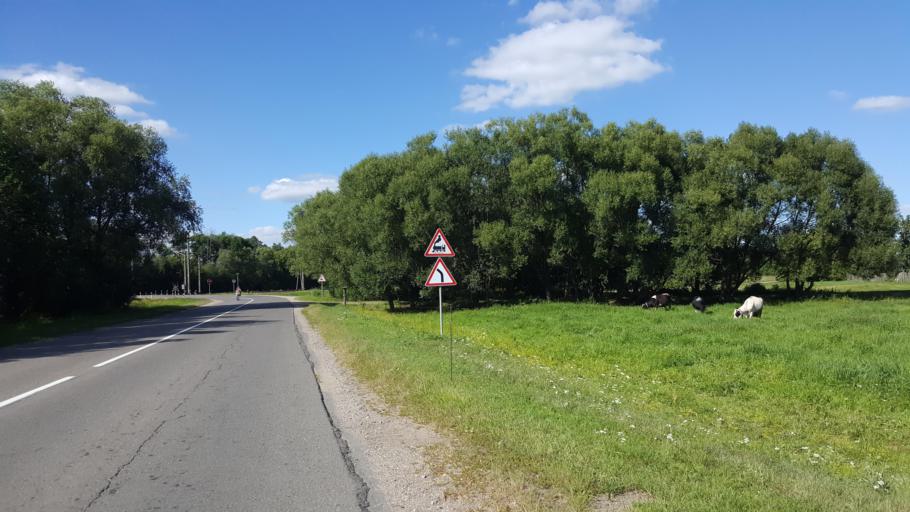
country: BY
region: Brest
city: Kobryn
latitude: 52.3415
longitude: 24.2399
